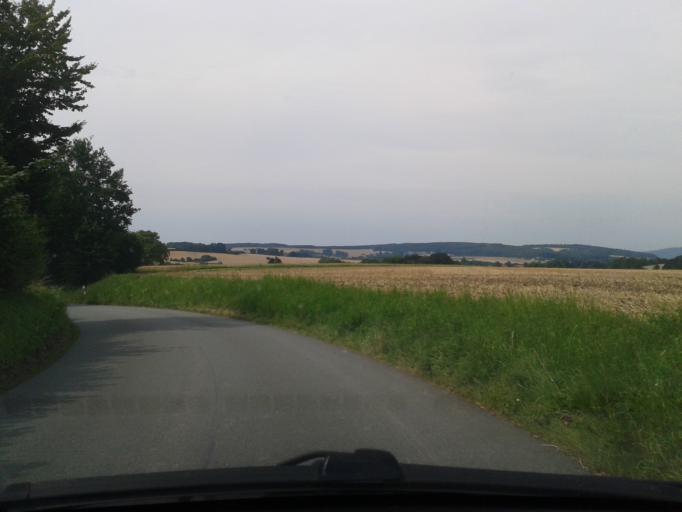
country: DE
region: North Rhine-Westphalia
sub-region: Regierungsbezirk Detmold
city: Barntrup
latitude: 51.9933
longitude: 9.1079
